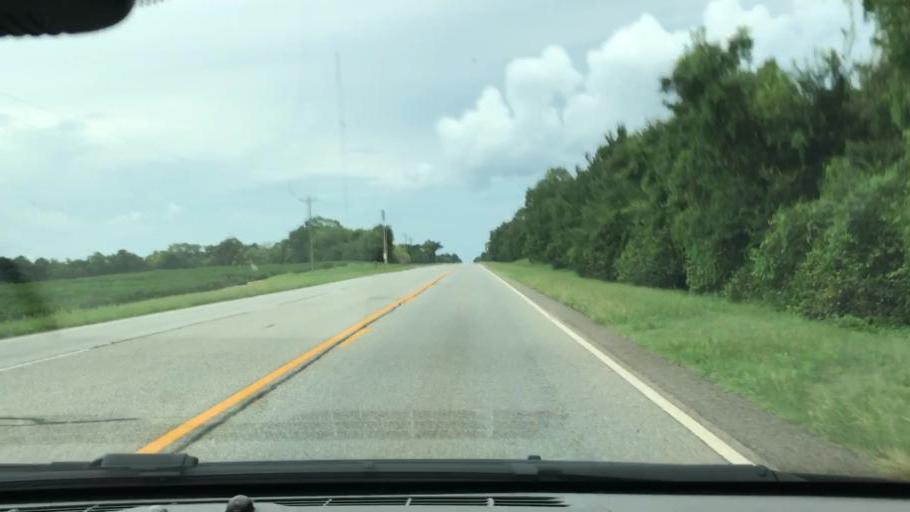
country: US
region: Georgia
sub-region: Early County
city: Blakely
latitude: 31.3028
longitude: -85.0523
